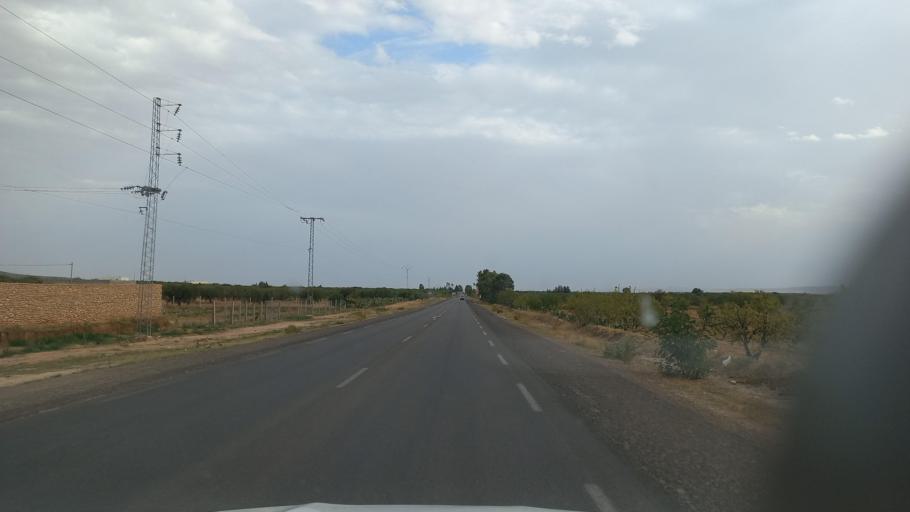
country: TN
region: Al Qasrayn
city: Sbiba
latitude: 35.3117
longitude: 9.0850
